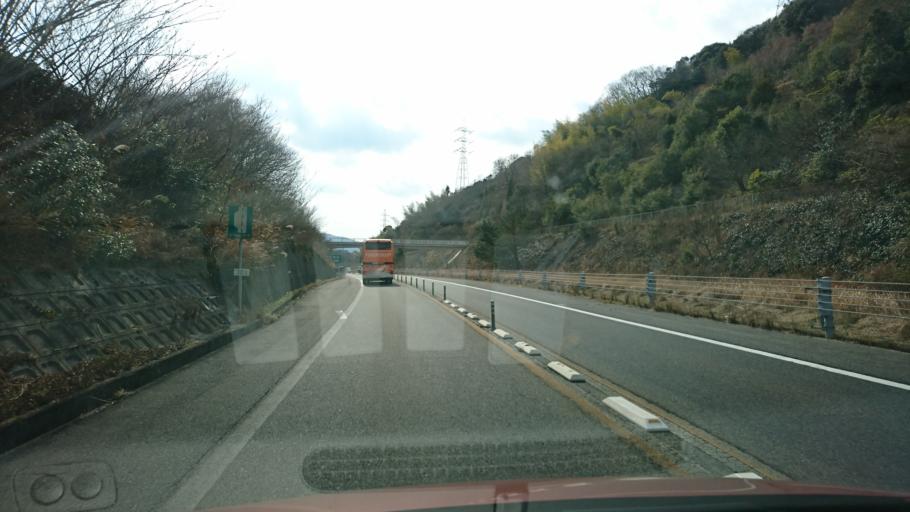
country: JP
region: Hiroshima
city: Innoshima
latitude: 34.2264
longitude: 133.0464
